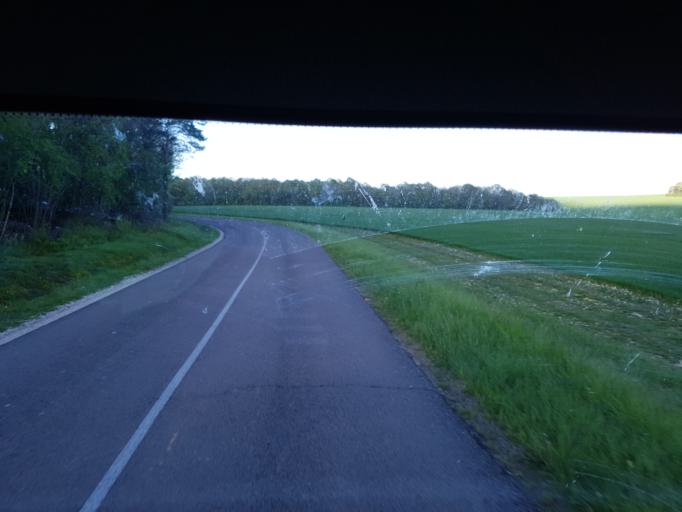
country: FR
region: Champagne-Ardenne
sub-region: Departement de l'Aube
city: Marigny-le-Chatel
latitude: 48.3267
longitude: 3.6354
